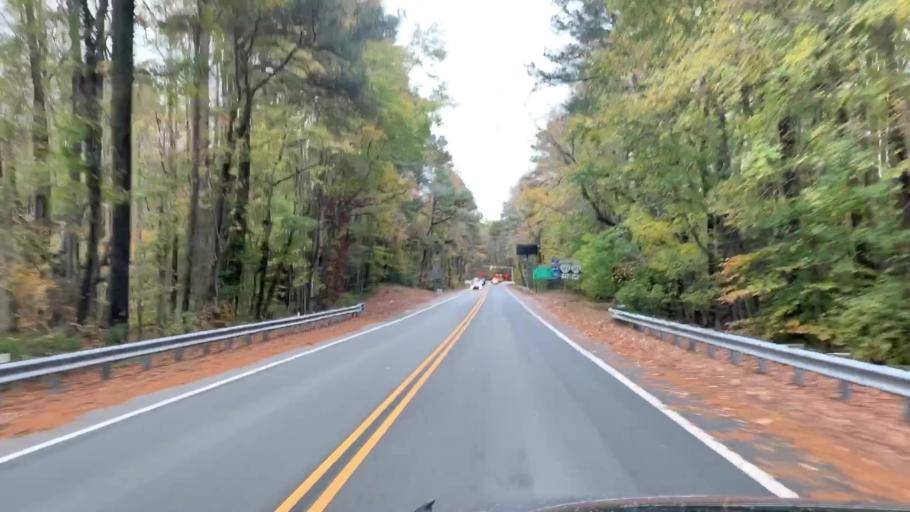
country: US
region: Virginia
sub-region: City of Williamsburg
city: Williamsburg
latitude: 37.2946
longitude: -76.6891
